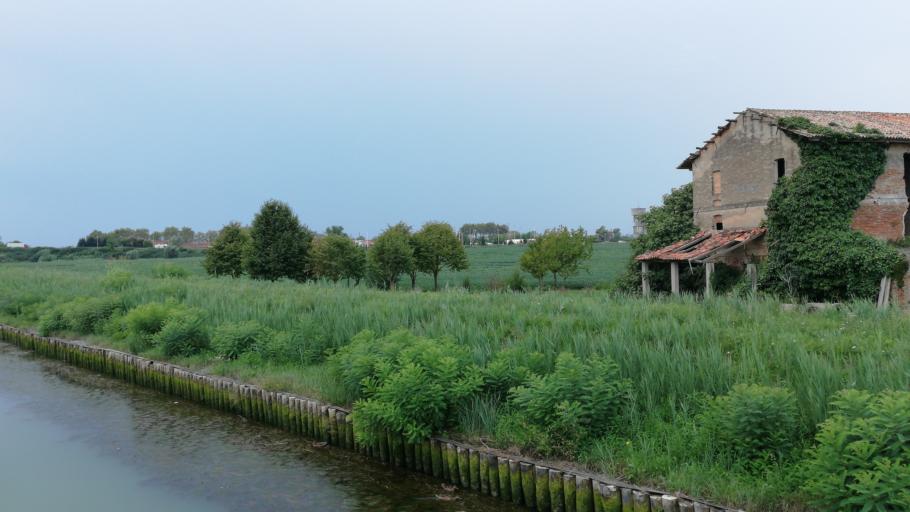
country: IT
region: Veneto
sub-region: Provincia di Venezia
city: Caorle
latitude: 45.6104
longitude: 12.8806
